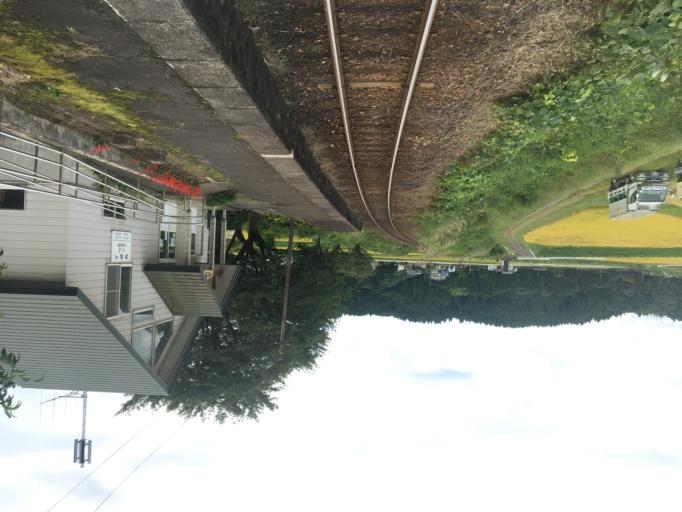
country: JP
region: Yamagata
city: Yuza
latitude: 39.2490
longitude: 140.1204
